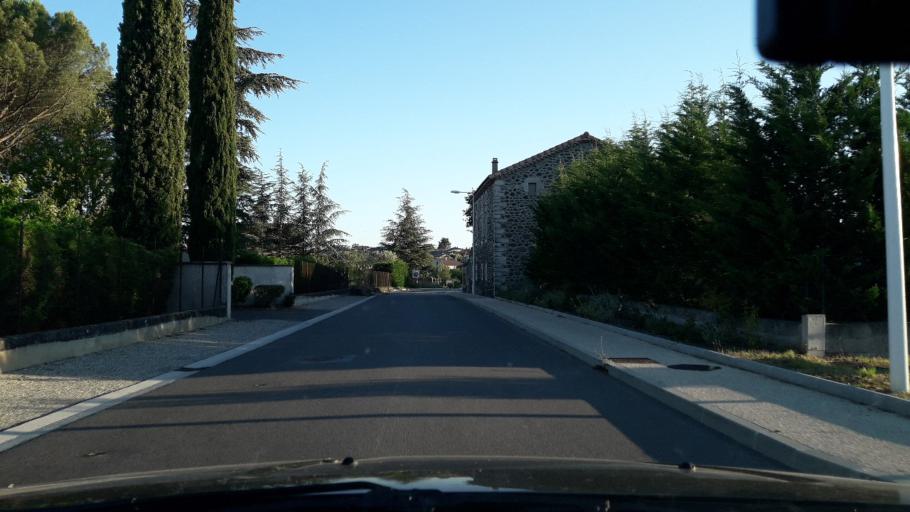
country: FR
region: Rhone-Alpes
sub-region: Departement de l'Ardeche
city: Lavilledieu
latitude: 44.5801
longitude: 4.4569
